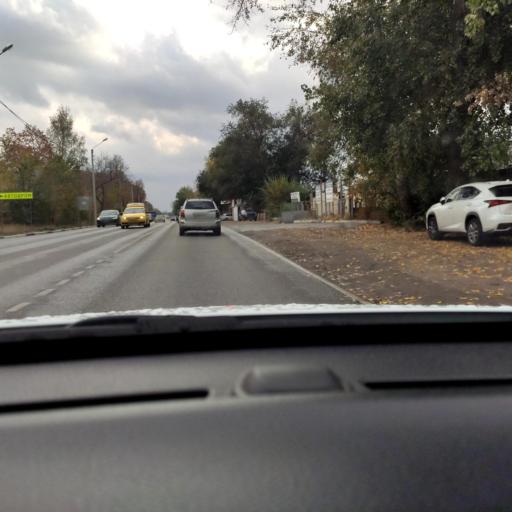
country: RU
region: Voronezj
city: Voronezh
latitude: 51.6714
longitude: 39.2719
